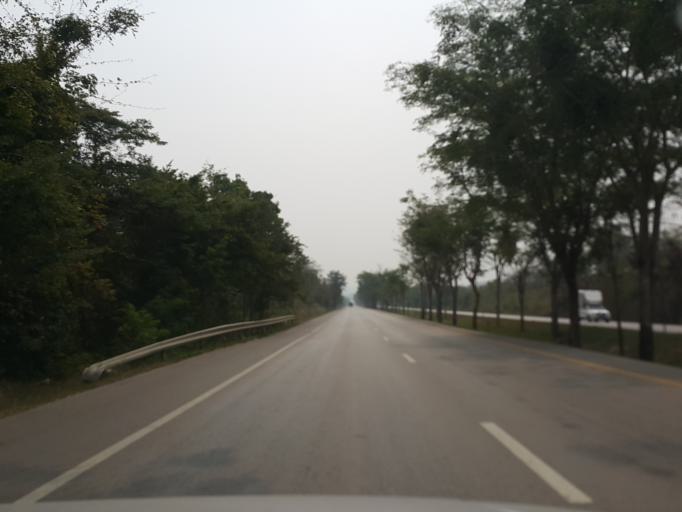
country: TH
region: Lampang
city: Ko Kha
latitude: 18.1239
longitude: 99.3926
